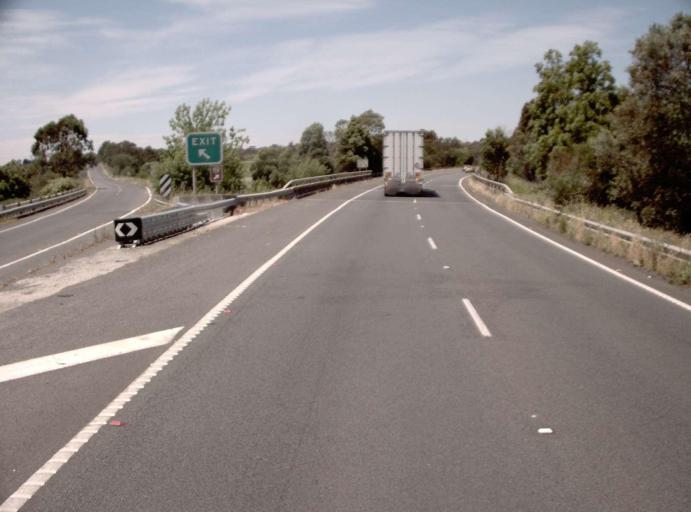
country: AU
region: Victoria
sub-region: Latrobe
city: Morwell
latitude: -38.2289
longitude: 146.3647
